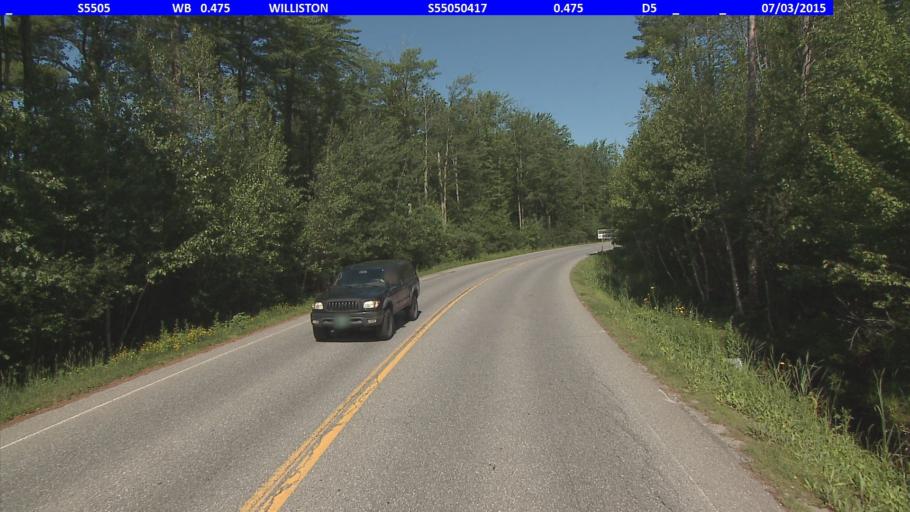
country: US
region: Vermont
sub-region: Chittenden County
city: South Burlington
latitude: 44.4468
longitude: -73.1333
